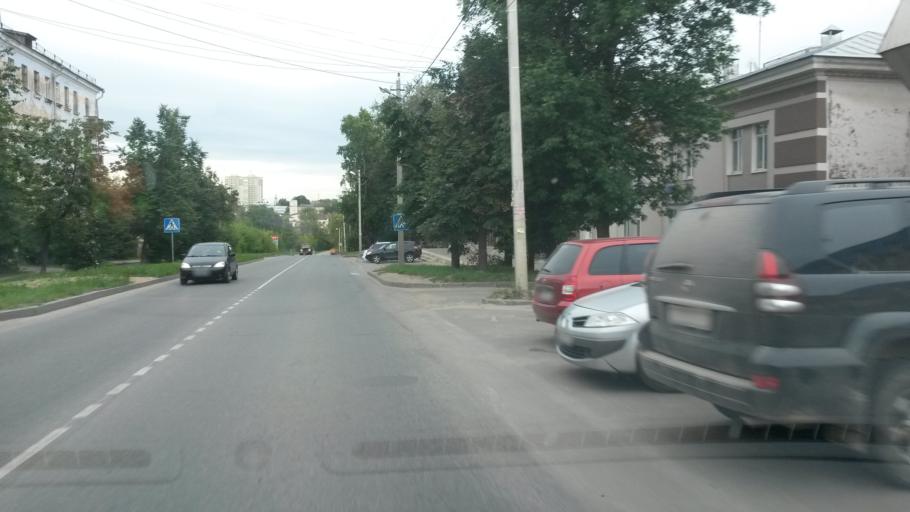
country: RU
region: Ivanovo
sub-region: Gorod Ivanovo
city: Ivanovo
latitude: 57.0169
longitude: 40.9570
